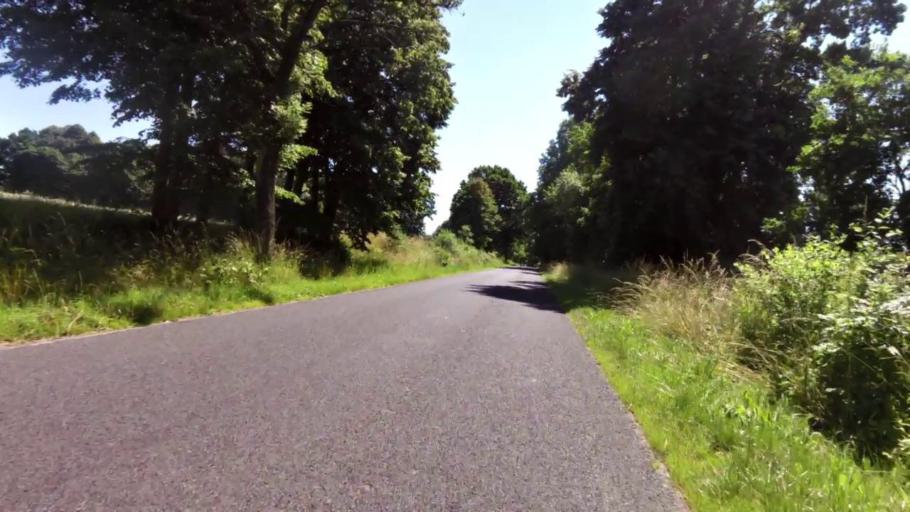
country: PL
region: West Pomeranian Voivodeship
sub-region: Powiat swidwinski
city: Rabino
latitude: 53.8472
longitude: 15.9907
